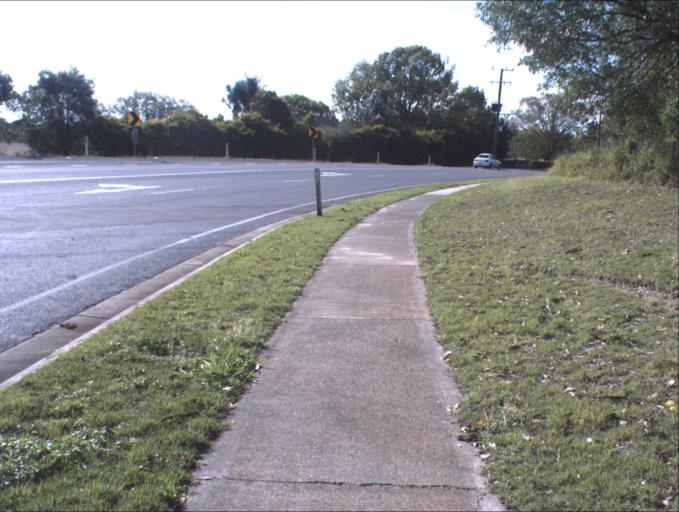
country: AU
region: Queensland
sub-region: Logan
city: Chambers Flat
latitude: -27.7606
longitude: 153.0912
